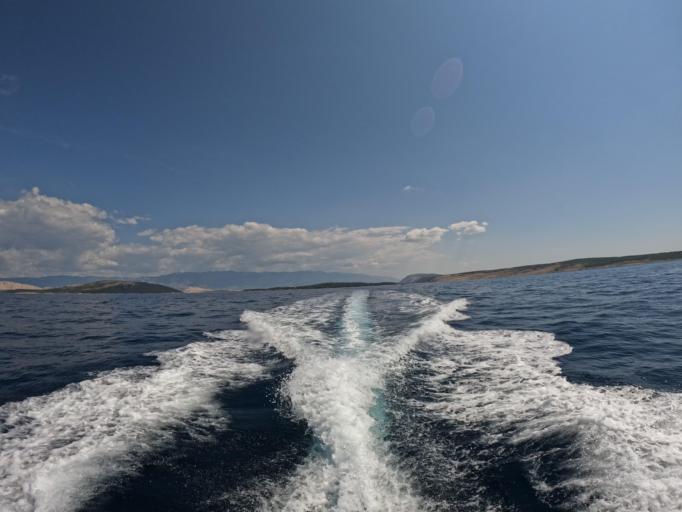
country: HR
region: Primorsko-Goranska
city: Lopar
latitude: 44.8631
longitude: 14.6901
